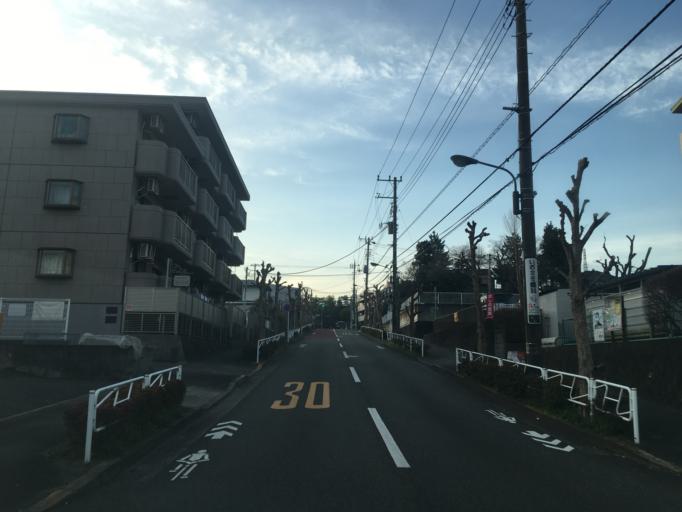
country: JP
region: Tokyo
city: Hino
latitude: 35.6241
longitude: 139.3930
